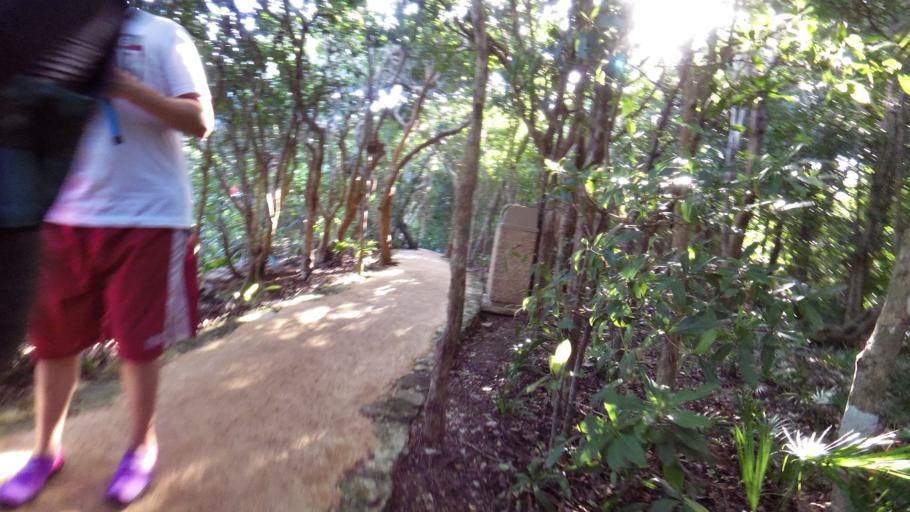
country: MX
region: Quintana Roo
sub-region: Tulum
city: Ciudad Chemuyil
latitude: 20.3170
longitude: -87.3605
